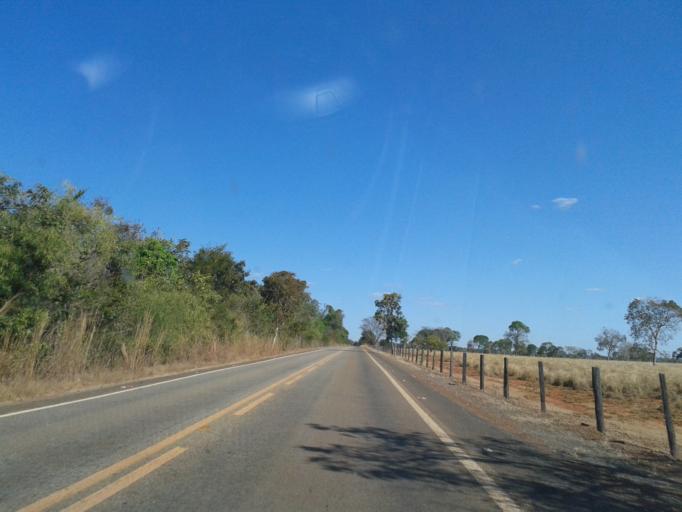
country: BR
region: Goias
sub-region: Mozarlandia
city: Mozarlandia
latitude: -14.2799
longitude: -50.4009
